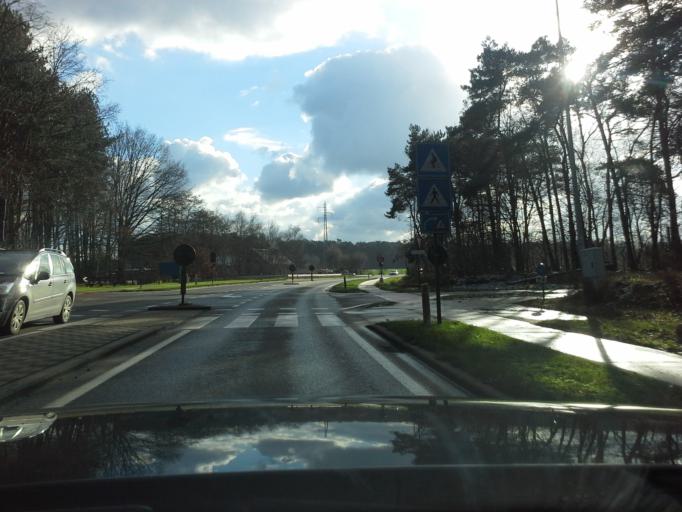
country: BE
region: Flanders
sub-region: Provincie Antwerpen
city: Mol
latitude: 51.1666
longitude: 5.1059
